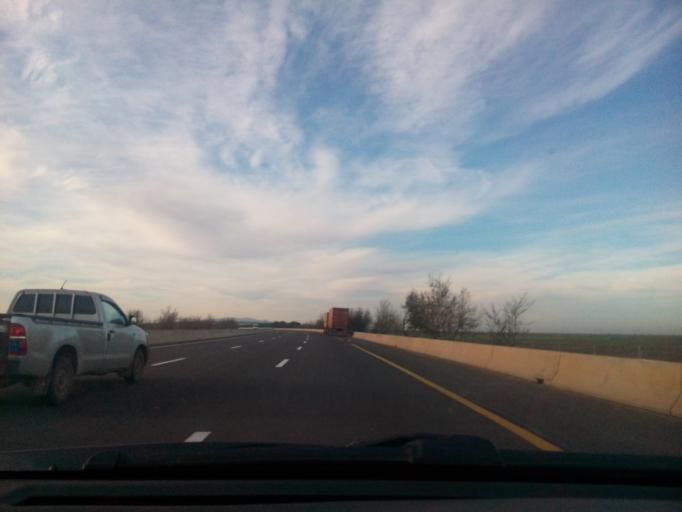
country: DZ
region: Mostaganem
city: Mostaganem
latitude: 35.6853
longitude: 0.1591
